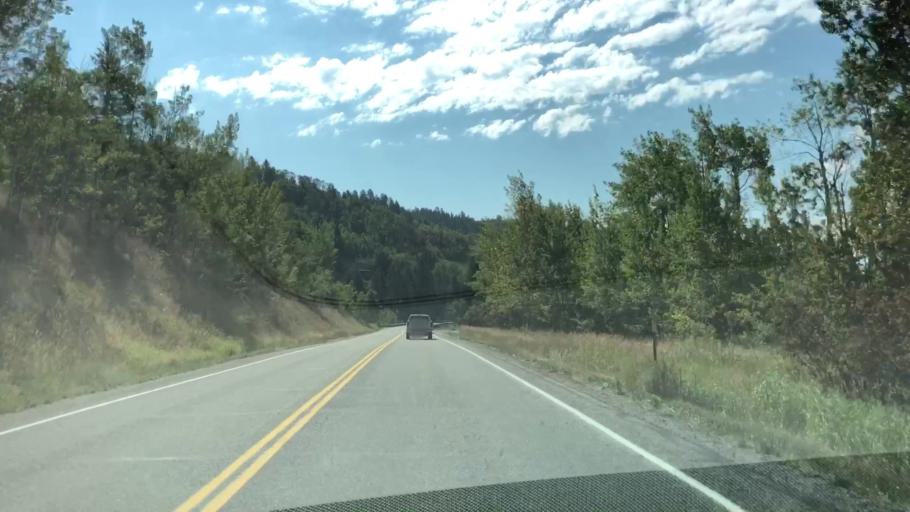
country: US
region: Idaho
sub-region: Teton County
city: Victor
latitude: 43.2797
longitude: -111.1170
